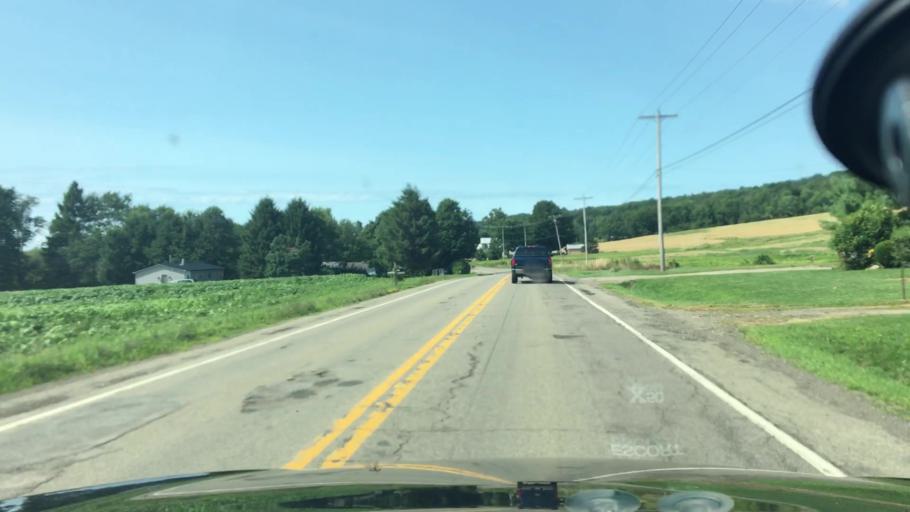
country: US
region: New York
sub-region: Chautauqua County
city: Brocton
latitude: 42.3065
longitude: -79.3531
